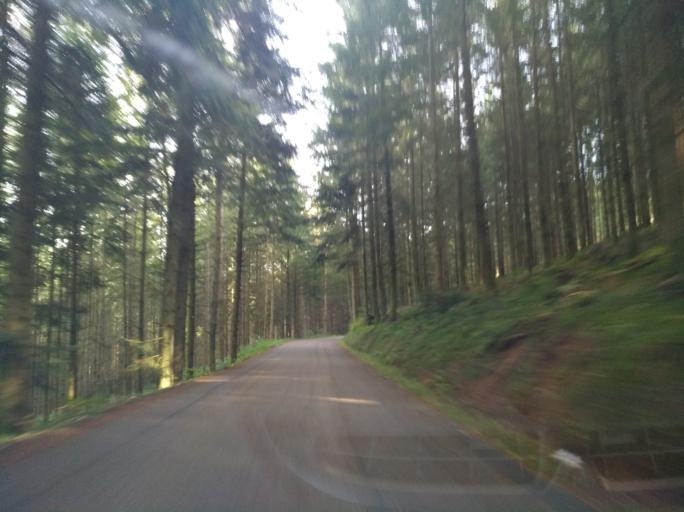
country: FR
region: Bourgogne
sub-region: Departement de Saone-et-Loire
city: Chauffailles
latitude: 46.2015
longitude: 4.3979
